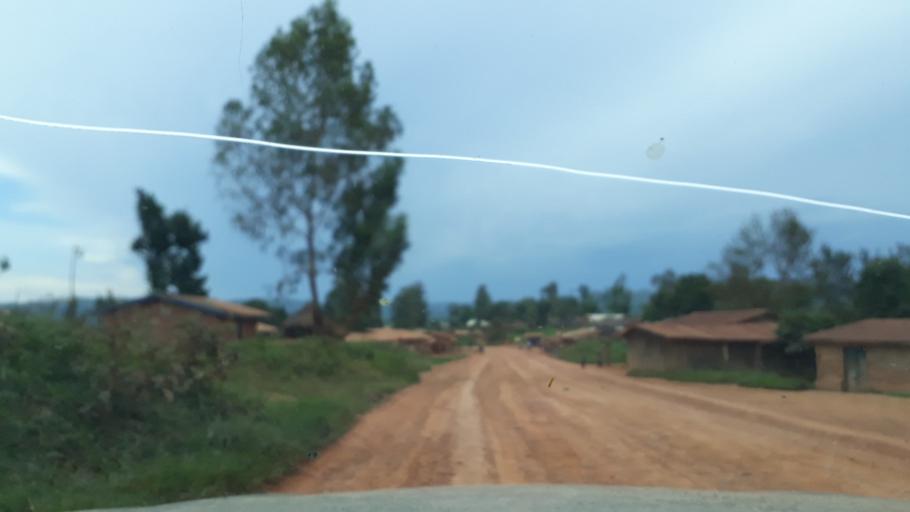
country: CD
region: Eastern Province
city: Bunia
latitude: 1.7941
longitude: 30.3865
